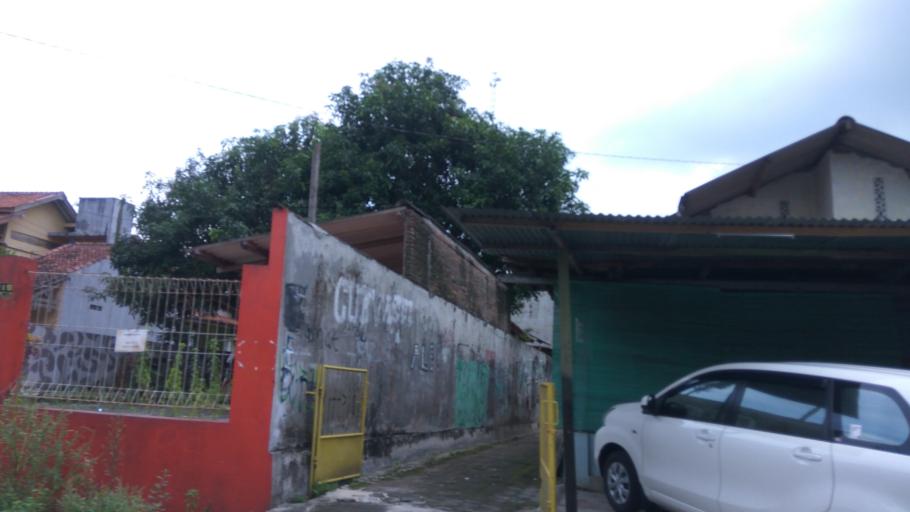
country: ID
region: Daerah Istimewa Yogyakarta
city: Melati
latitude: -7.7206
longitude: 110.4040
